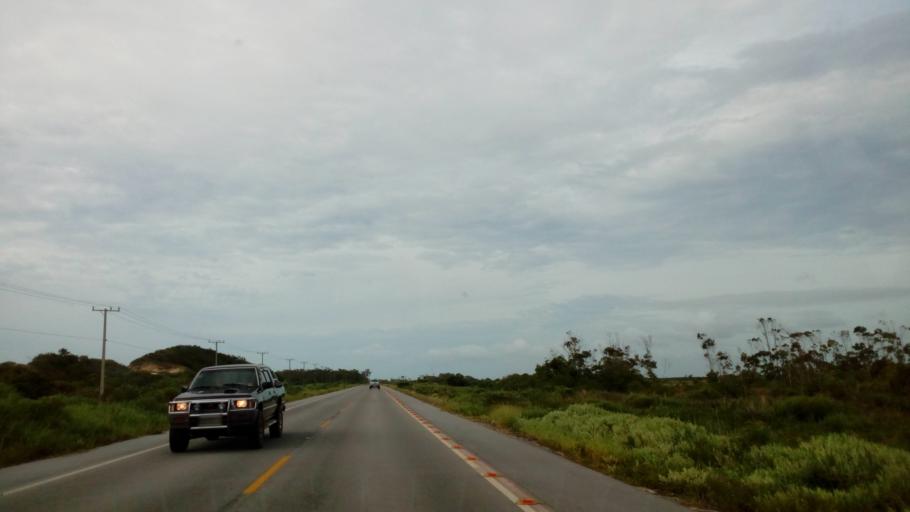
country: BR
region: Santa Catarina
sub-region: Laguna
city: Laguna
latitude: -28.5422
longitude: -48.7900
